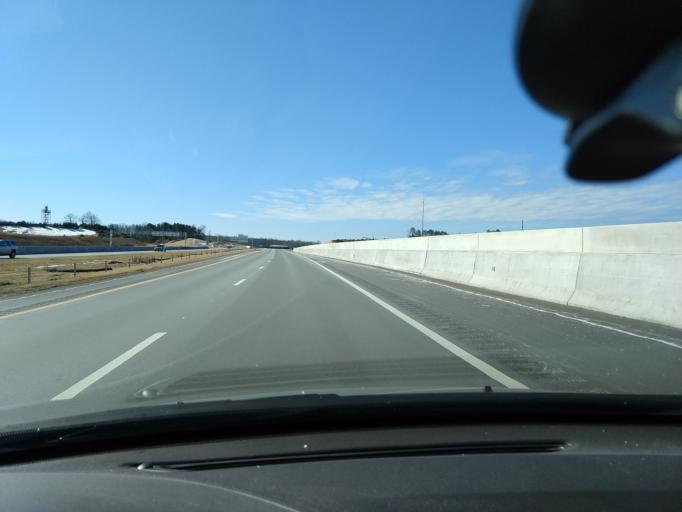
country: US
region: North Carolina
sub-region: Guilford County
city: Oak Ridge
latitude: 36.1225
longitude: -79.9373
